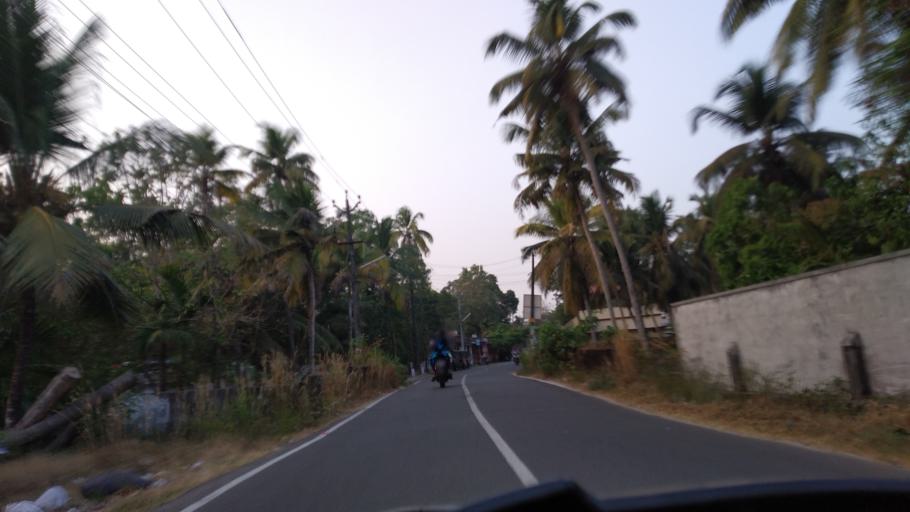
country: IN
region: Kerala
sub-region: Ernakulam
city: Elur
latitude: 10.1229
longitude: 76.2391
